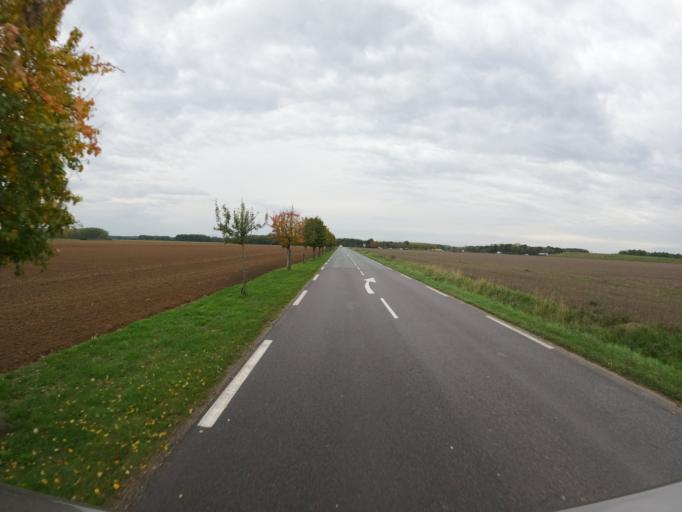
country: FR
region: Ile-de-France
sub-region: Departement de Seine-et-Marne
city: Villeneuve-le-Comte
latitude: 48.8165
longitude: 2.8239
